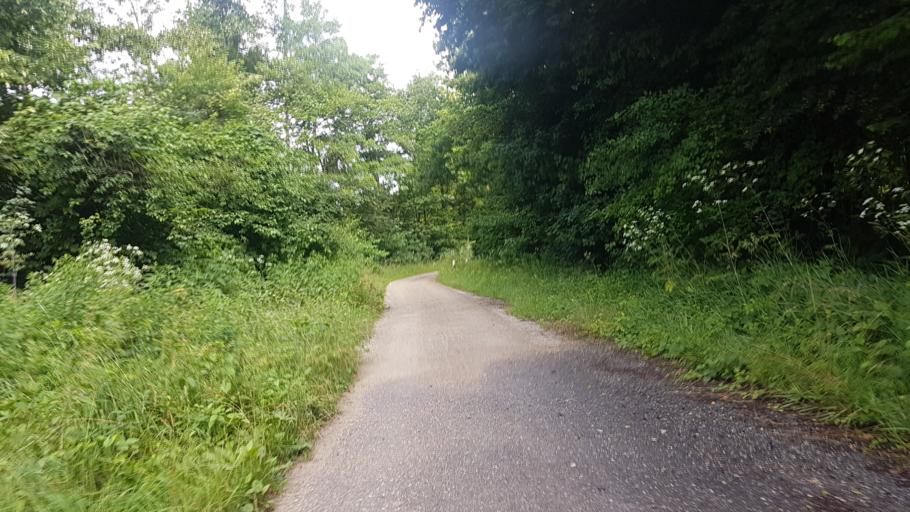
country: DE
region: Bavaria
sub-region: Lower Bavaria
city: Essing
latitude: 48.9448
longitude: 11.7446
